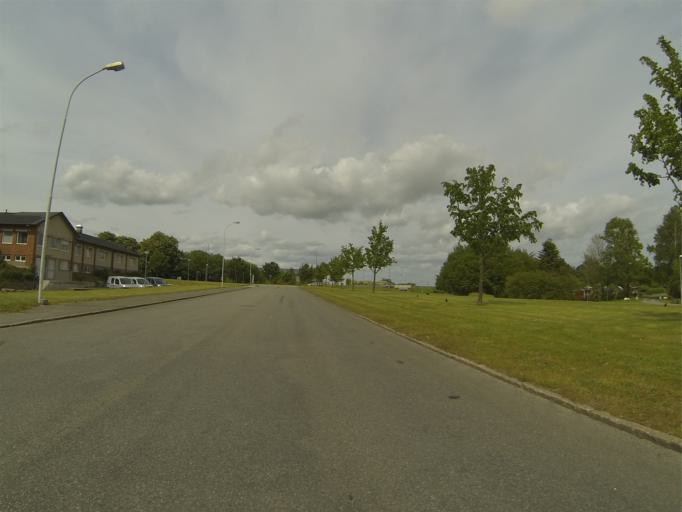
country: SE
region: Skane
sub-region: Tomelilla Kommun
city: Tomelilla
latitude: 55.5468
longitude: 13.9573
